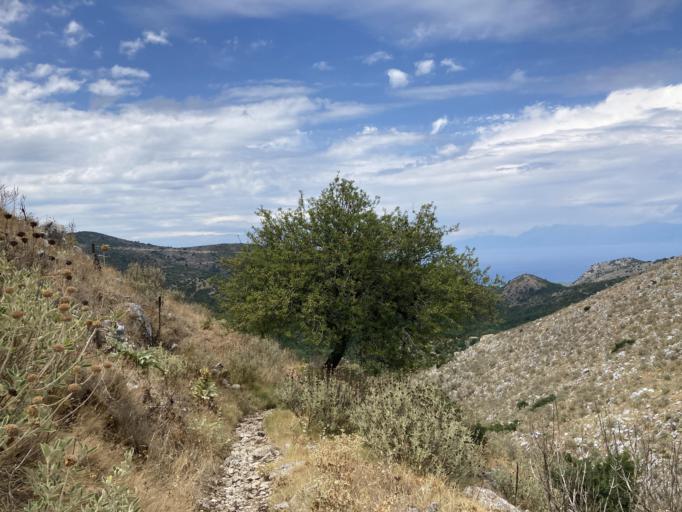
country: GR
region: Ionian Islands
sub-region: Nomos Kerkyras
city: Acharavi
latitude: 39.7598
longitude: 19.8793
